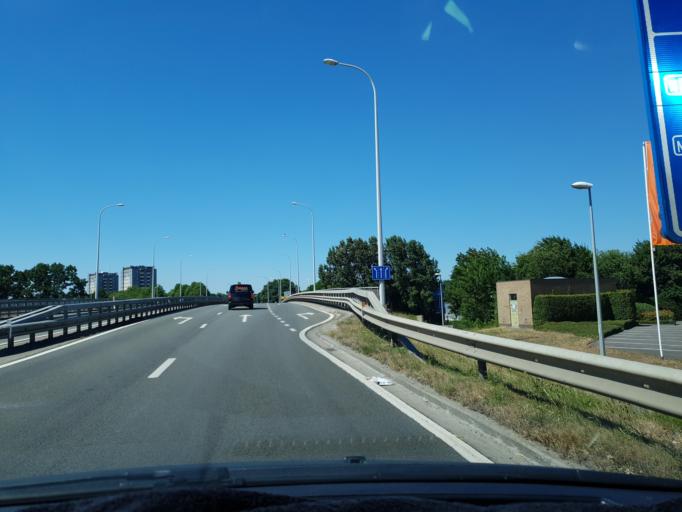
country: BE
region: Flanders
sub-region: Provincie Antwerpen
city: Herentals
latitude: 51.1696
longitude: 4.8479
